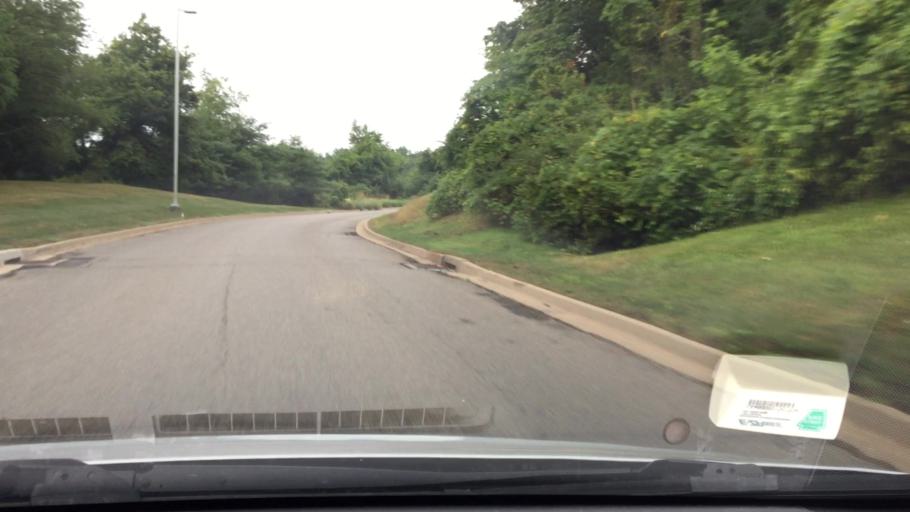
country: US
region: Pennsylvania
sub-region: Butler County
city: Cranberry Township
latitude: 40.6602
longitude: -80.0981
